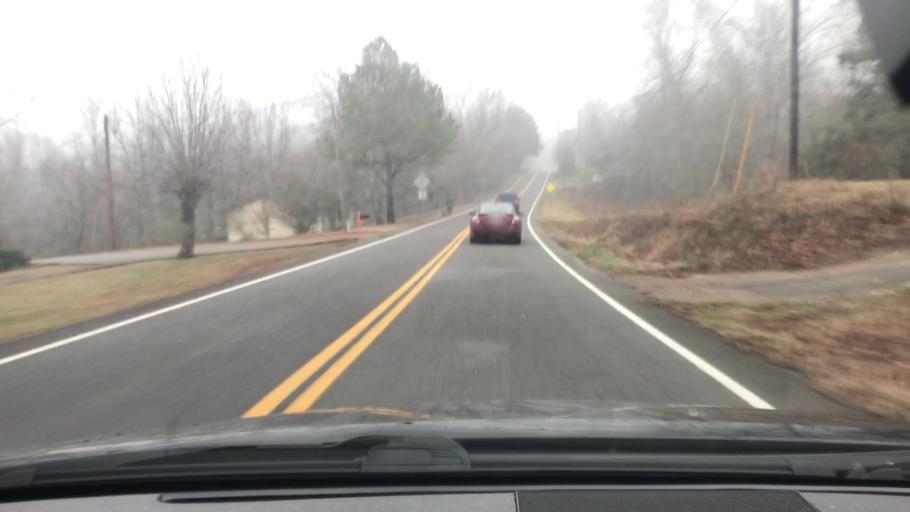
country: US
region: Tennessee
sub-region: Cheatham County
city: Ashland City
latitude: 36.2766
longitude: -87.1875
